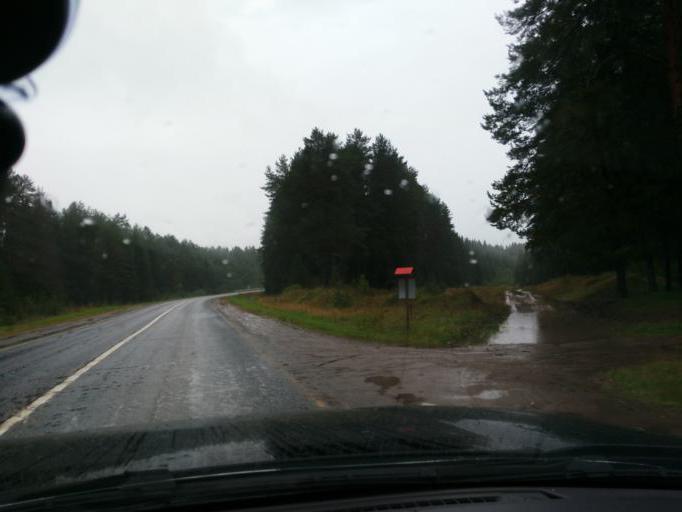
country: RU
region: Perm
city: Yugo-Kamskiy
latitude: 57.5594
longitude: 55.6818
